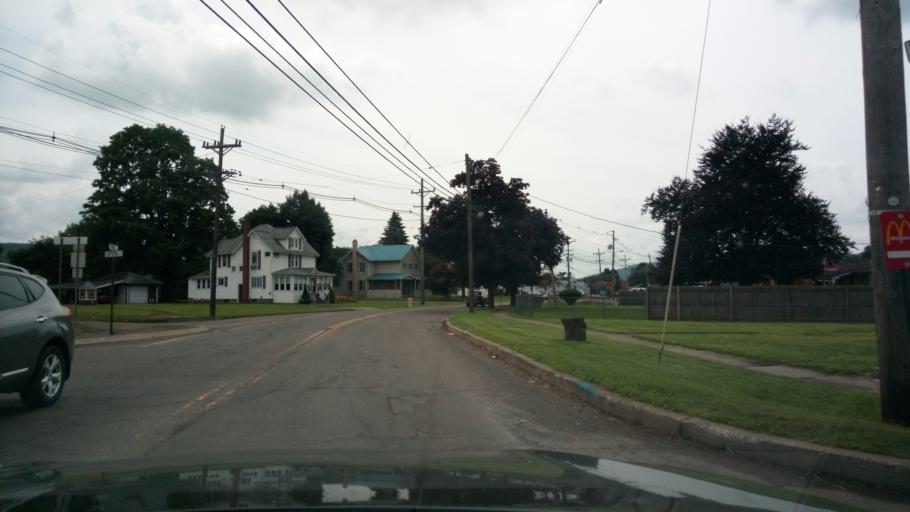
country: US
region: Pennsylvania
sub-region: Bradford County
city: South Waverly
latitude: 41.9940
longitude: -76.5215
